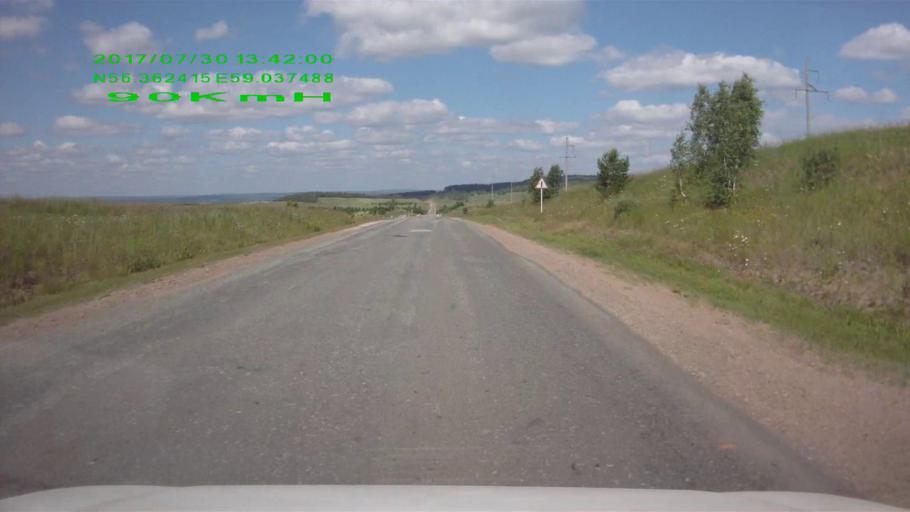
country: RU
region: Sverdlovsk
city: Mikhaylovsk
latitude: 56.3629
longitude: 59.0376
